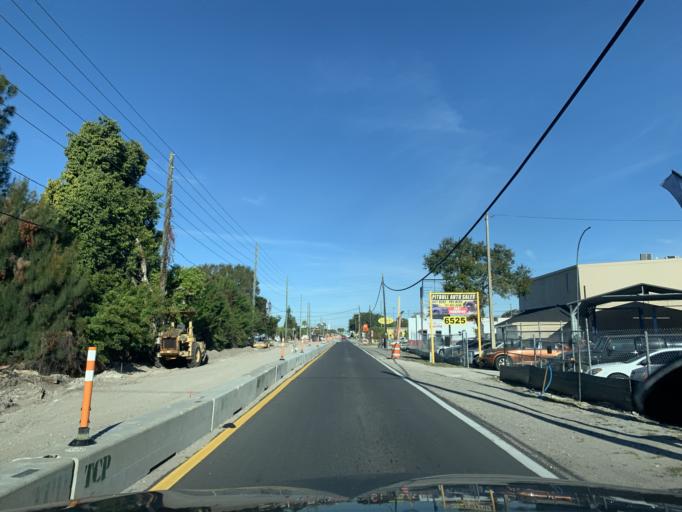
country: US
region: Florida
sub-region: Pinellas County
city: Lealman
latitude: 27.8311
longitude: -82.6779
